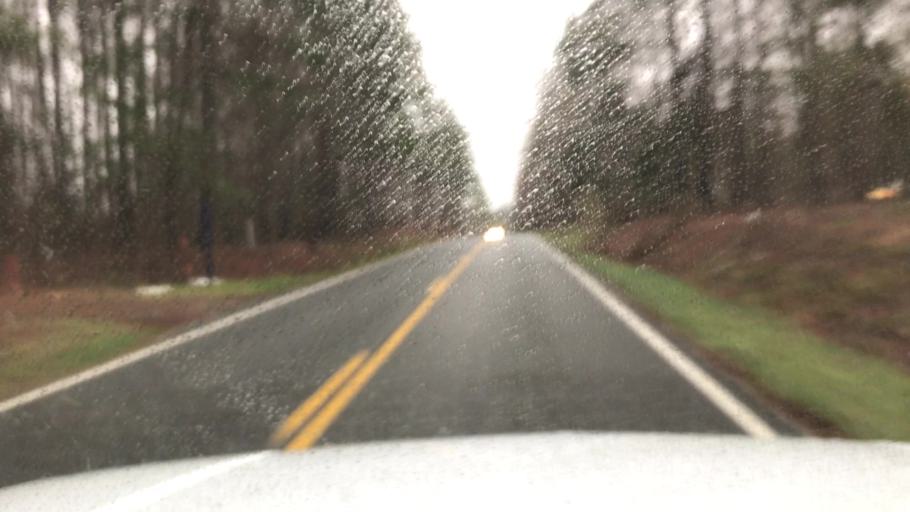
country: US
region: Virginia
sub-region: Henrico County
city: Short Pump
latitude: 37.6570
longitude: -77.6784
